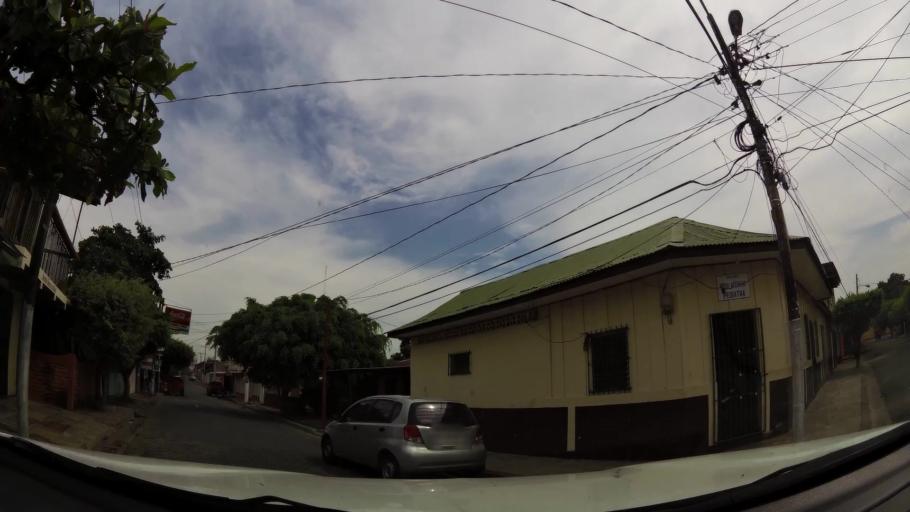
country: NI
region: Rivas
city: Rivas
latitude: 11.4419
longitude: -85.8283
